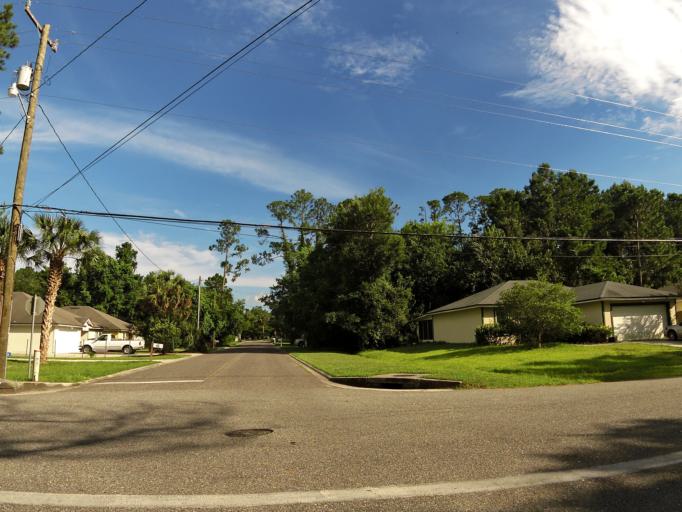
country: US
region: Florida
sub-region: Clay County
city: Green Cove Springs
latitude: 29.9897
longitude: -81.6943
